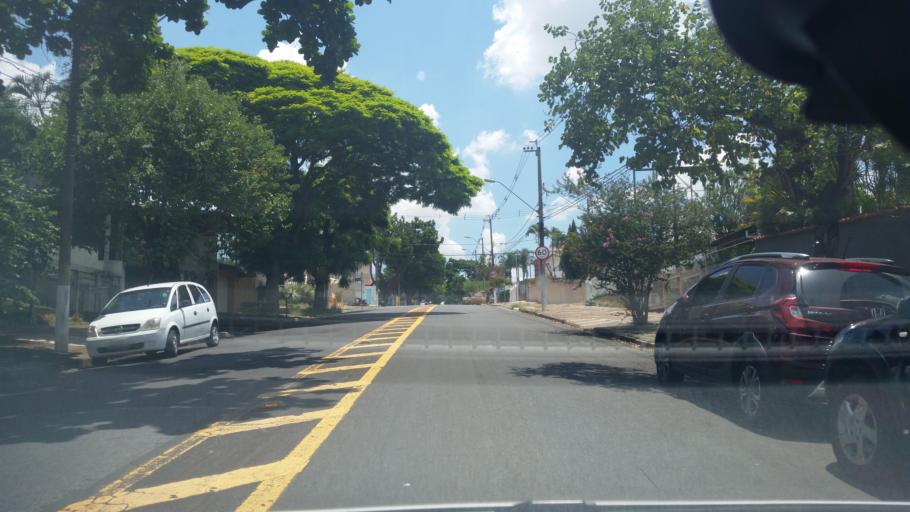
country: BR
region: Sao Paulo
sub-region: Campinas
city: Campinas
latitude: -22.8772
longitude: -47.0523
